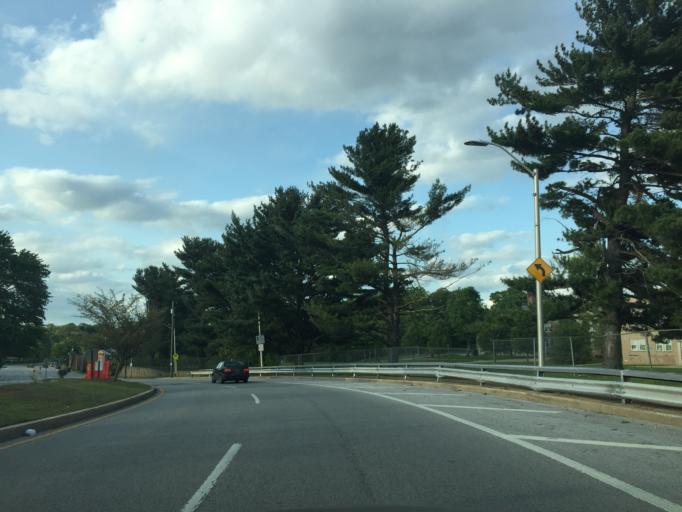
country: US
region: Maryland
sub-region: Baltimore County
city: Overlea
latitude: 39.3515
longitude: -76.5429
